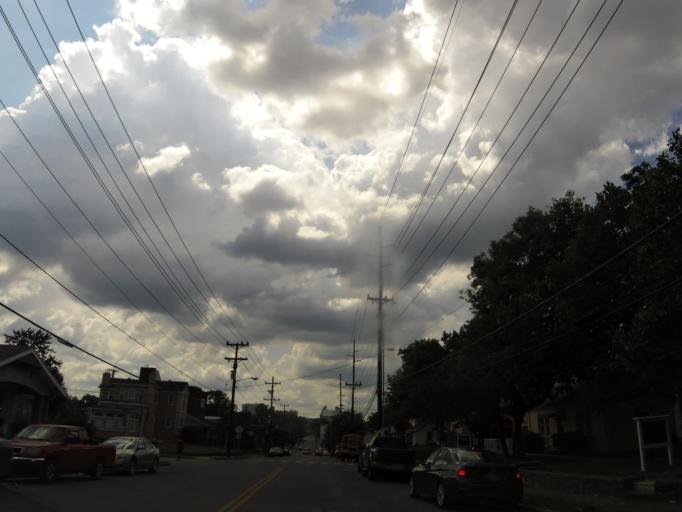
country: US
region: Tennessee
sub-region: Davidson County
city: Nashville
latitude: 36.1431
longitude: -86.7902
